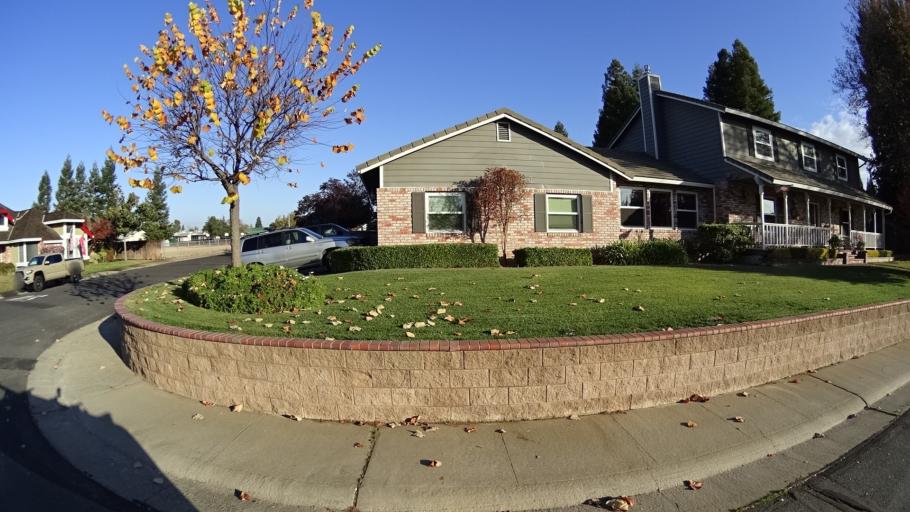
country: US
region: California
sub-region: Sacramento County
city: Citrus Heights
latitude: 38.7193
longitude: -121.2519
